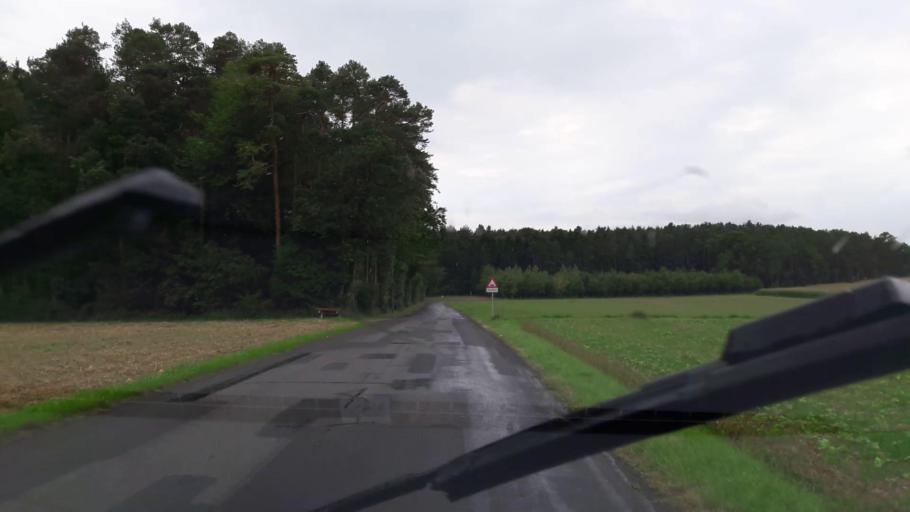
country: AT
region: Styria
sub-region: Politischer Bezirk Hartberg-Fuerstenfeld
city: Sankt Johann in der Haide
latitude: 47.2719
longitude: 16.0216
